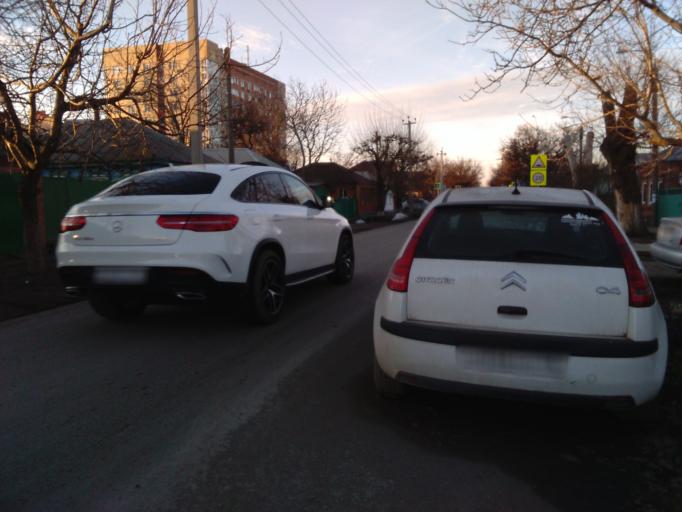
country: RU
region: Rostov
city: Bataysk
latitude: 47.1423
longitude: 39.7442
